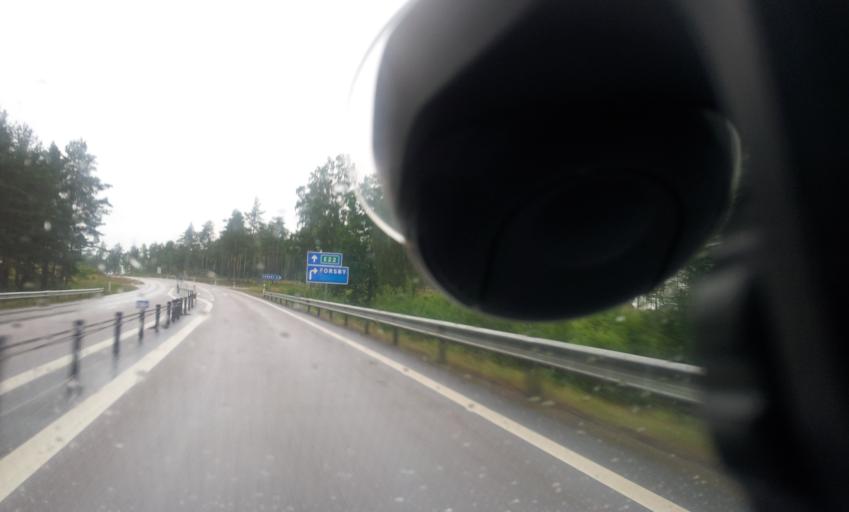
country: SE
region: Kalmar
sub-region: Vasterviks Kommun
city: Forserum
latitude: 58.0561
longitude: 16.5287
